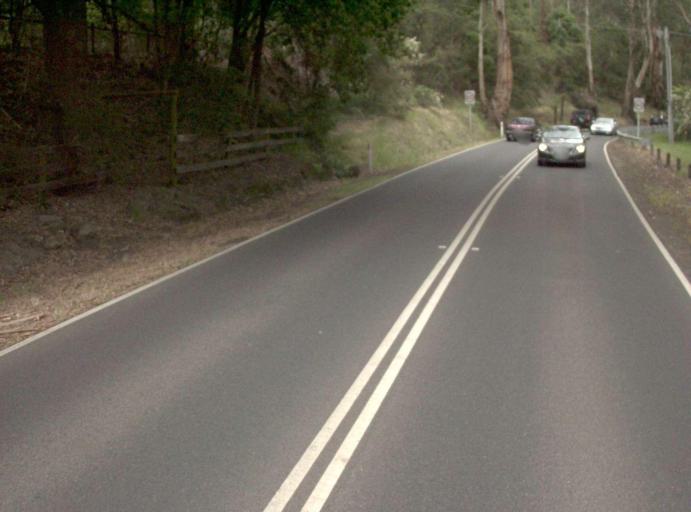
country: AU
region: Victoria
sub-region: Yarra Ranges
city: Millgrove
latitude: -37.7562
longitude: 145.6777
